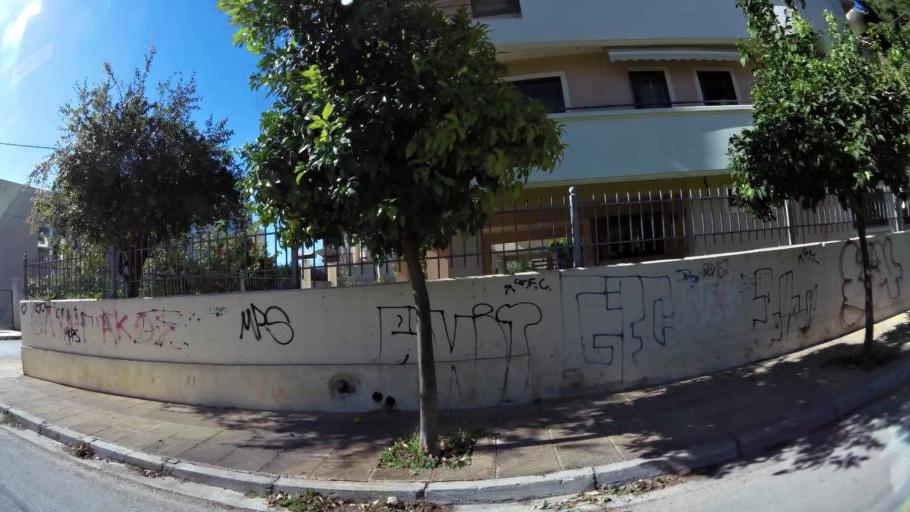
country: GR
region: Attica
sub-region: Nomarchia Athinas
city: Khalandrion
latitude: 38.0232
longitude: 23.8167
